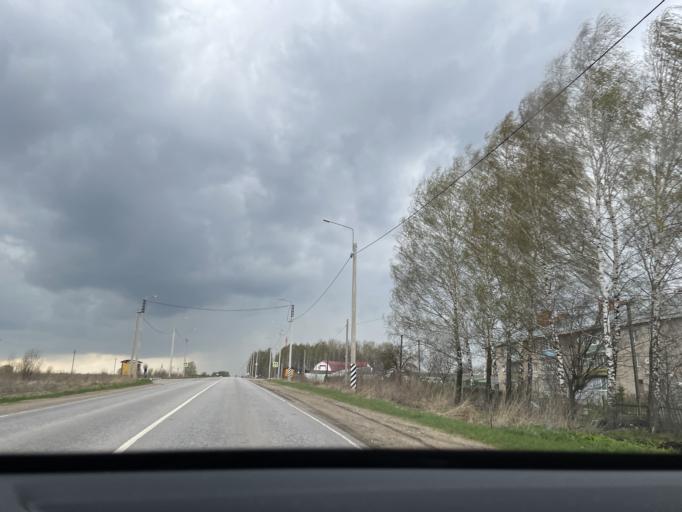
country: RU
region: Tula
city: Novogurovskiy
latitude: 54.5250
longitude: 37.4173
